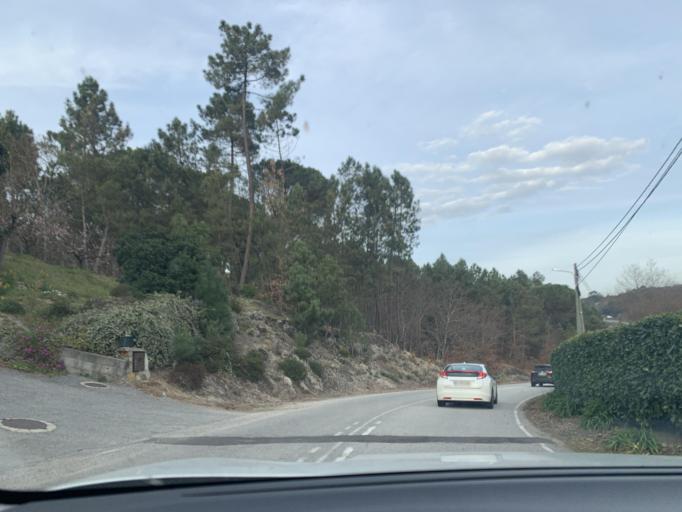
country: PT
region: Viseu
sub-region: Viseu
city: Viseu
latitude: 40.6019
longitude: -7.9876
